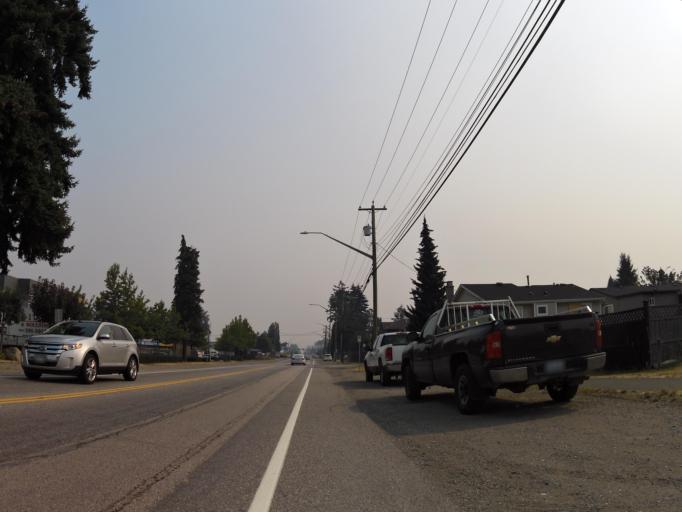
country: CA
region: British Columbia
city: Delta
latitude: 49.1482
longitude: -122.8730
